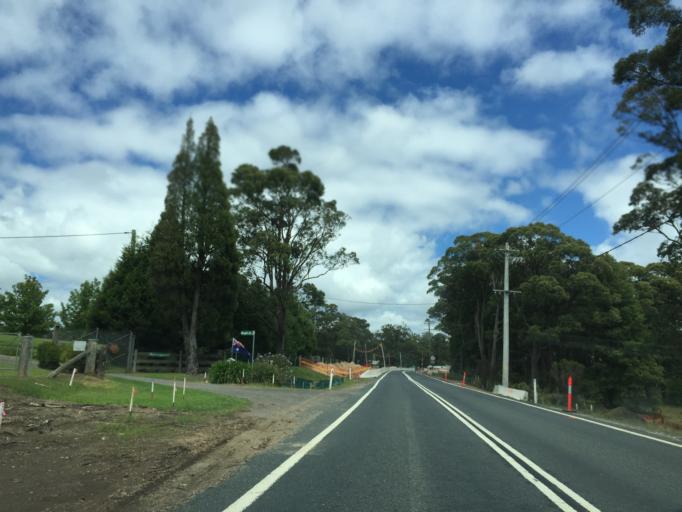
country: AU
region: New South Wales
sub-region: Hawkesbury
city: Richmond
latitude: -33.5157
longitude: 150.6056
